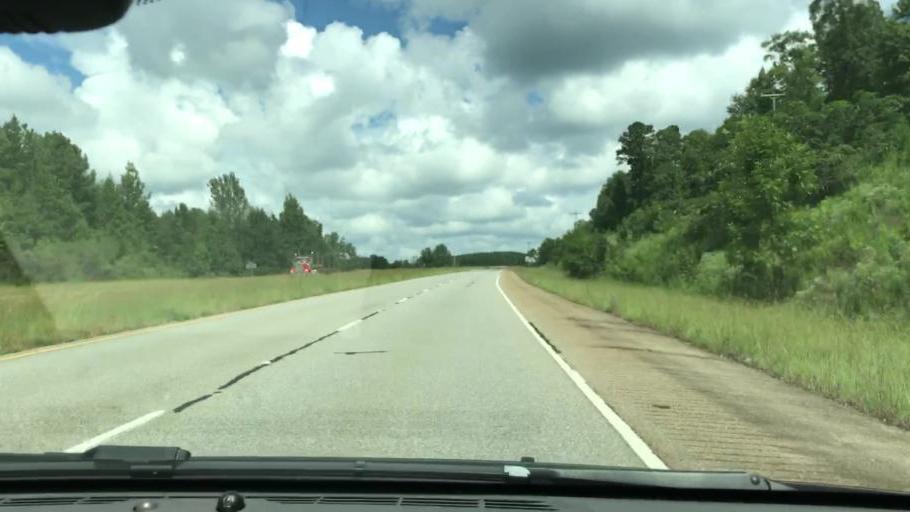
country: US
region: Georgia
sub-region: Stewart County
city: Lumpkin
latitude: 32.1063
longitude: -84.8130
